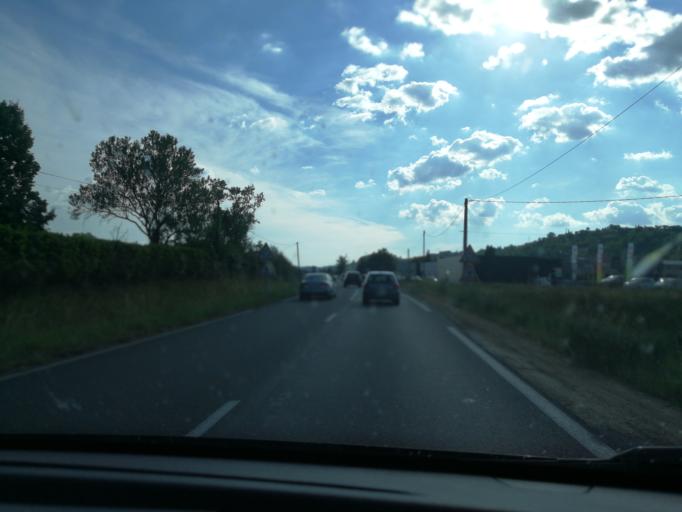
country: FR
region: Midi-Pyrenees
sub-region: Departement du Tarn
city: Cagnac-les-Mines
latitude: 43.9617
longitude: 2.1694
